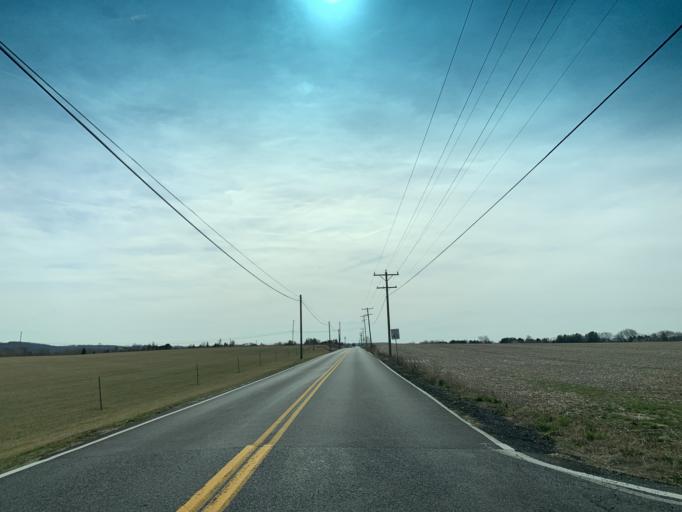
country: US
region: Maryland
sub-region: Frederick County
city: Adamstown
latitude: 39.3029
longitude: -77.4637
